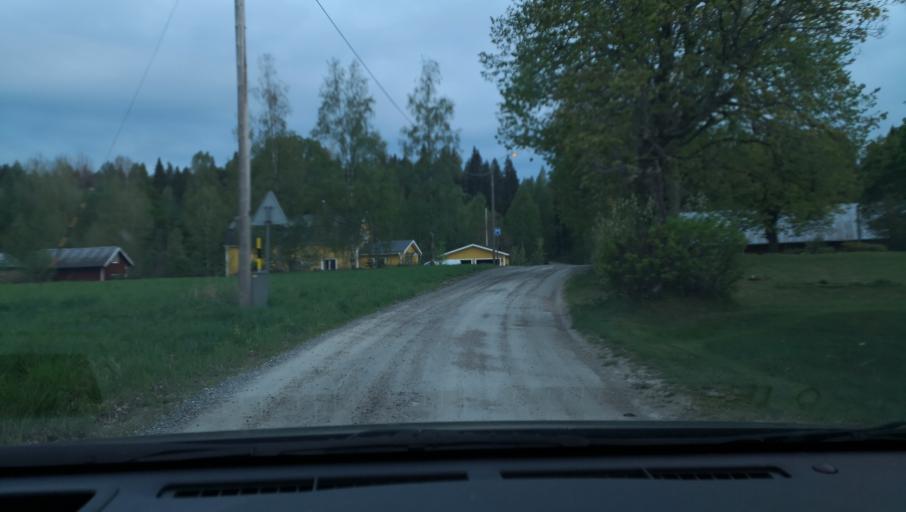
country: SE
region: Vaestmanland
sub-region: Skinnskattebergs Kommun
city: Skinnskatteberg
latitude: 59.7424
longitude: 15.4706
